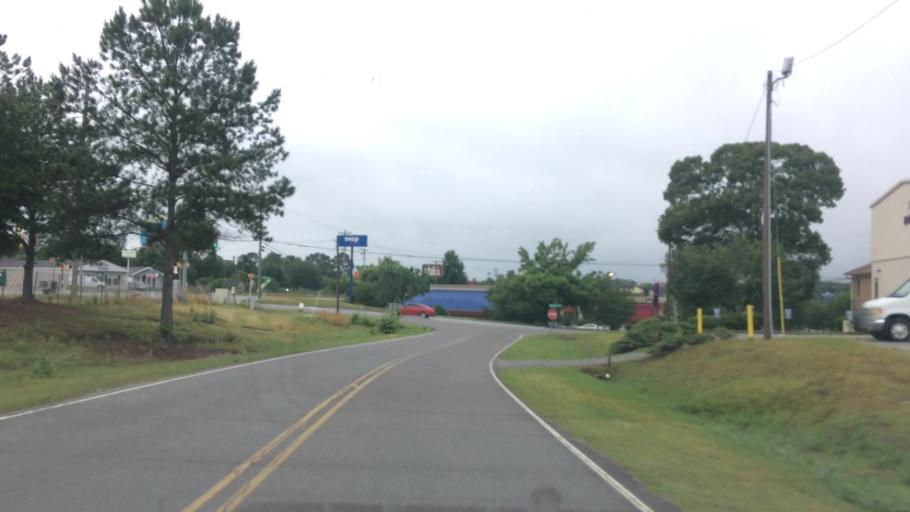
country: US
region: South Carolina
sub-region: Richland County
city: Dentsville
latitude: 34.0801
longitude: -80.9424
